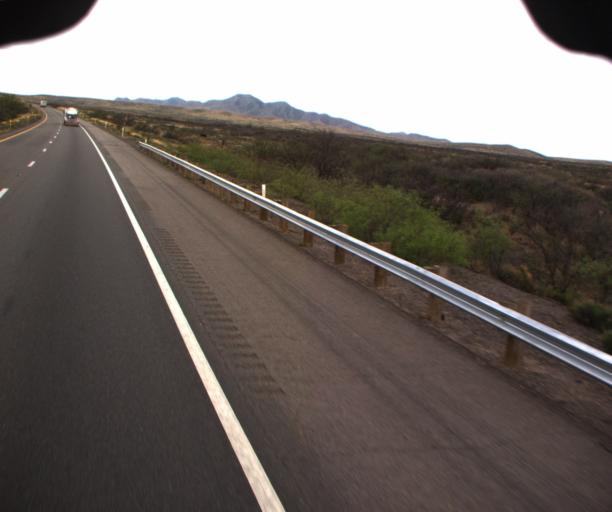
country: US
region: Arizona
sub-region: Cochise County
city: Willcox
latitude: 32.1523
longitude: -109.9902
